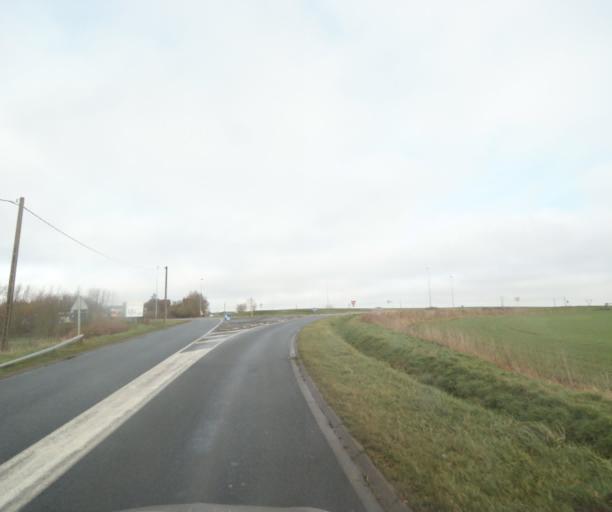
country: FR
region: Nord-Pas-de-Calais
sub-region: Departement du Nord
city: Famars
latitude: 50.2992
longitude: 3.5162
